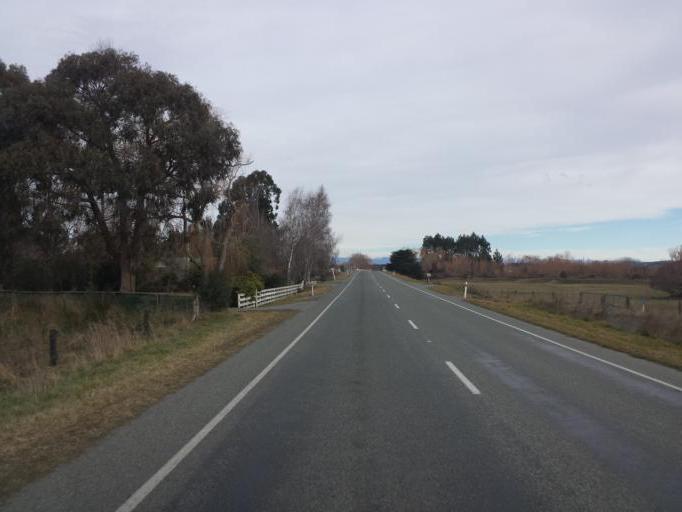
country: NZ
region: Canterbury
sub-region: Timaru District
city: Pleasant Point
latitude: -44.1146
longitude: 171.2136
